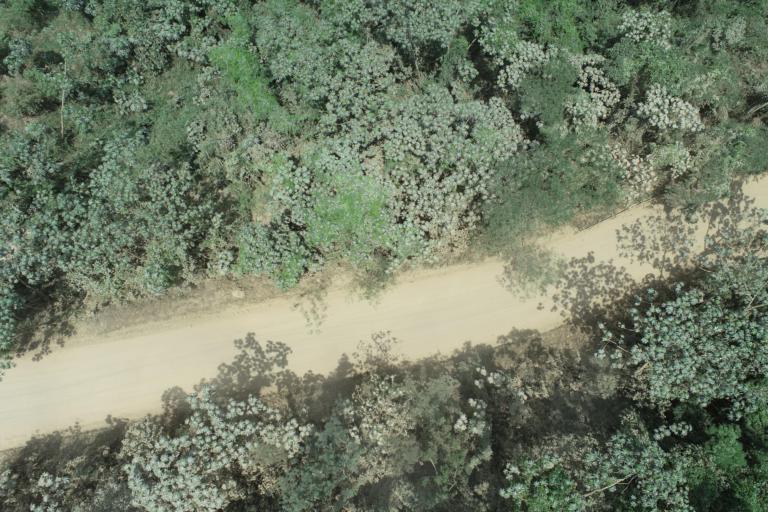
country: BO
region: La Paz
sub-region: Provincia Larecaja
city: Guanay
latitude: -15.7666
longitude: -67.6628
